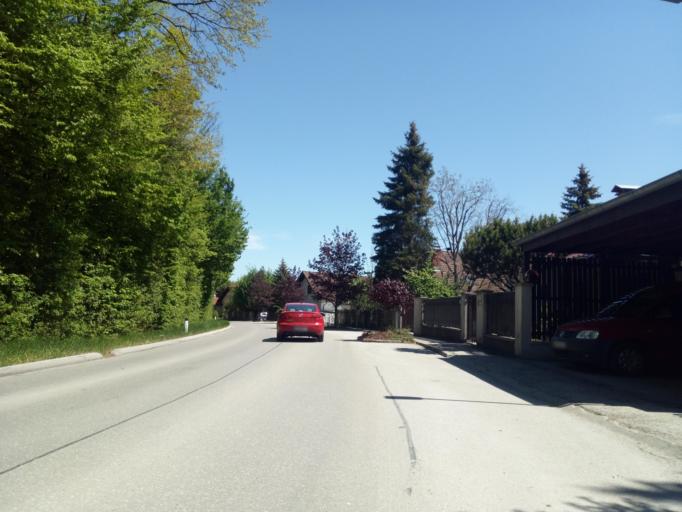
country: AT
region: Lower Austria
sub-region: Politischer Bezirk Modling
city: Kaltenleutgeben
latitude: 48.1304
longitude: 16.1916
